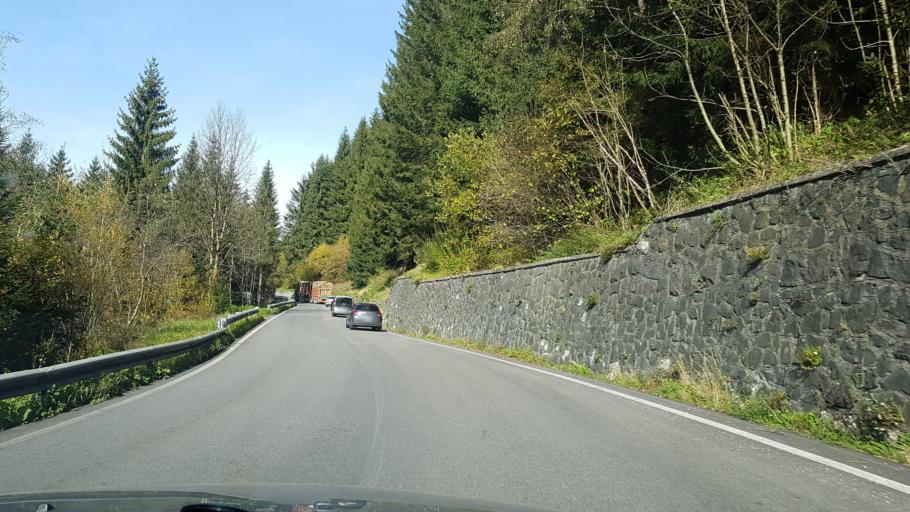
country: IT
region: Veneto
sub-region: Provincia di Belluno
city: San Nicolo Comelico
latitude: 46.5698
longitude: 12.5373
